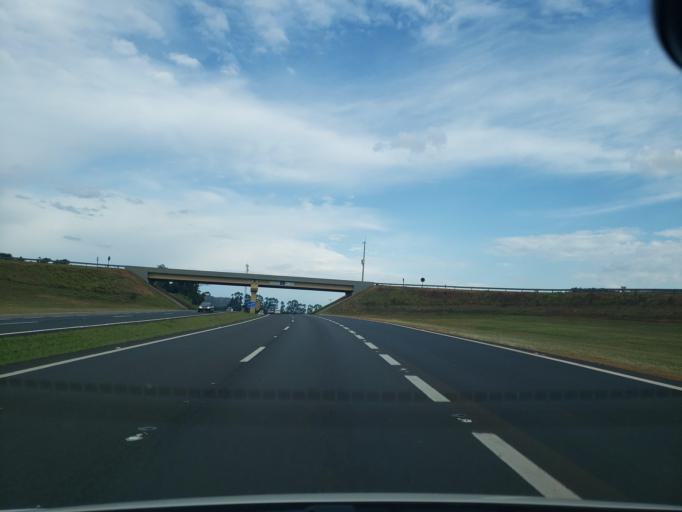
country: BR
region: Sao Paulo
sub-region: Itirapina
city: Itirapina
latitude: -22.2680
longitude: -47.9341
